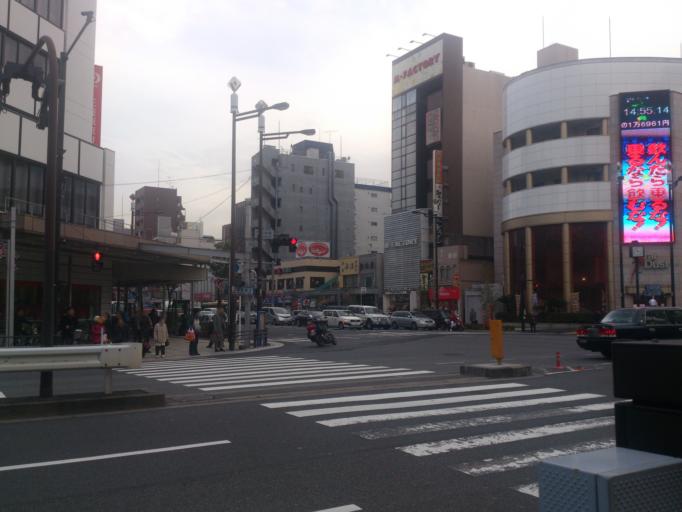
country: JP
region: Tokyo
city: Urayasu
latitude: 35.6728
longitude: 139.7949
